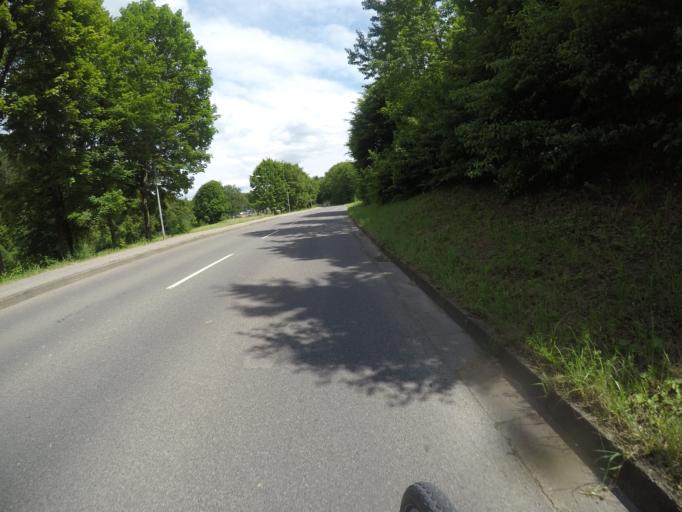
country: DE
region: Baden-Wuerttemberg
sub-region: Regierungsbezirk Stuttgart
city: Waldenbuch
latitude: 48.6351
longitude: 9.1497
